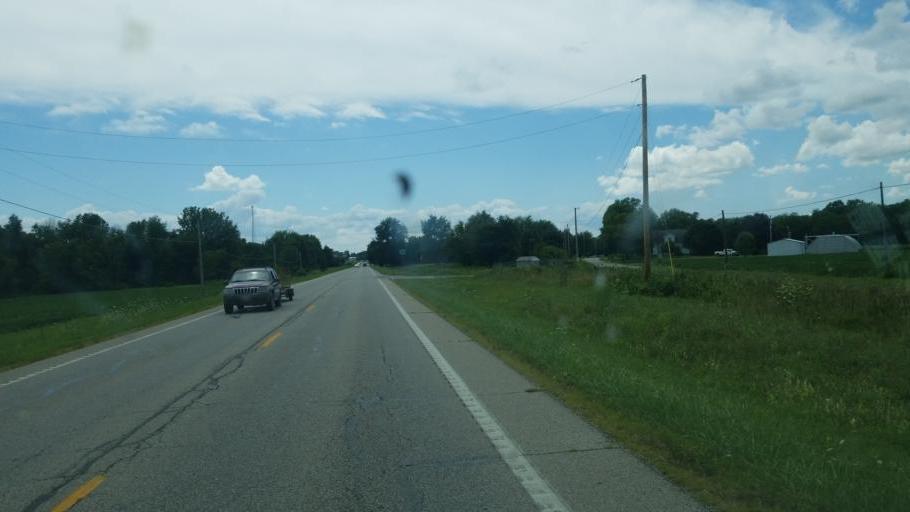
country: US
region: Ohio
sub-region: Delaware County
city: Sunbury
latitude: 40.2672
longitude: -82.7769
